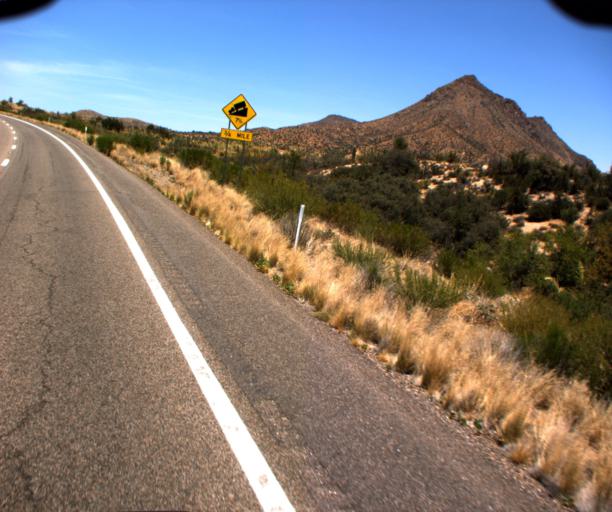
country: US
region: Arizona
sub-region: Gila County
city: Miami
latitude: 33.5305
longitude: -110.9156
